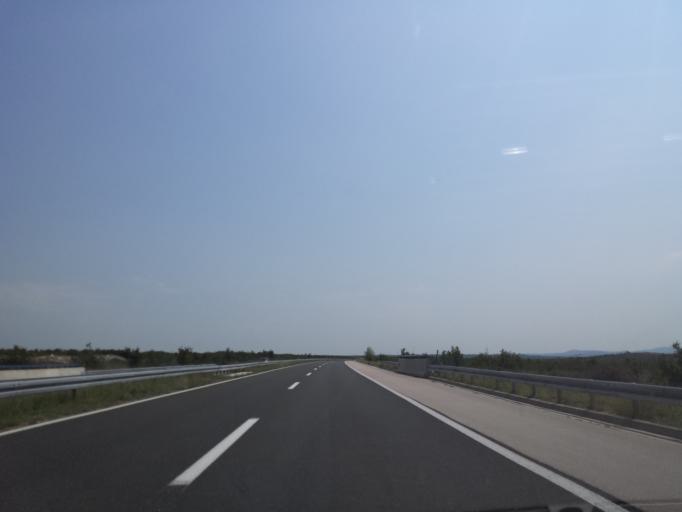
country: HR
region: Zadarska
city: Polaca
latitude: 44.0392
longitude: 15.5559
